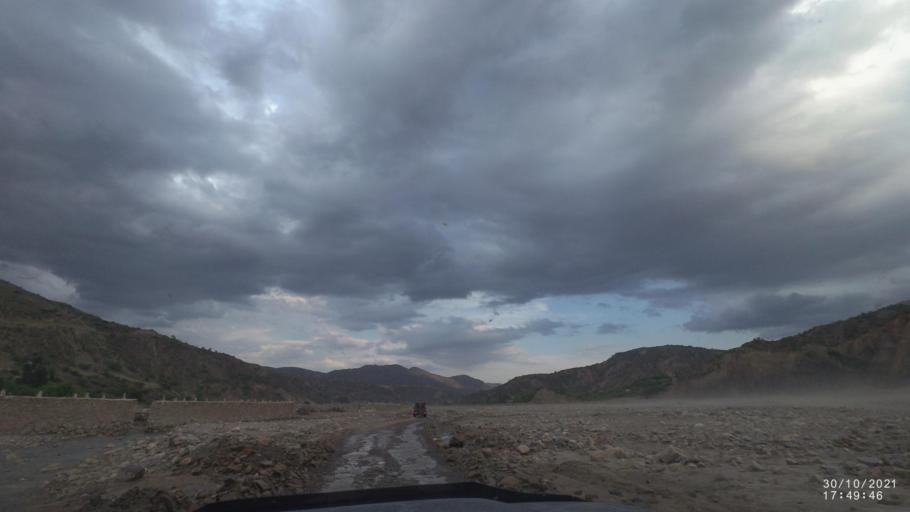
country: BO
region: Cochabamba
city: Sipe Sipe
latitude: -17.5362
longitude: -66.5130
